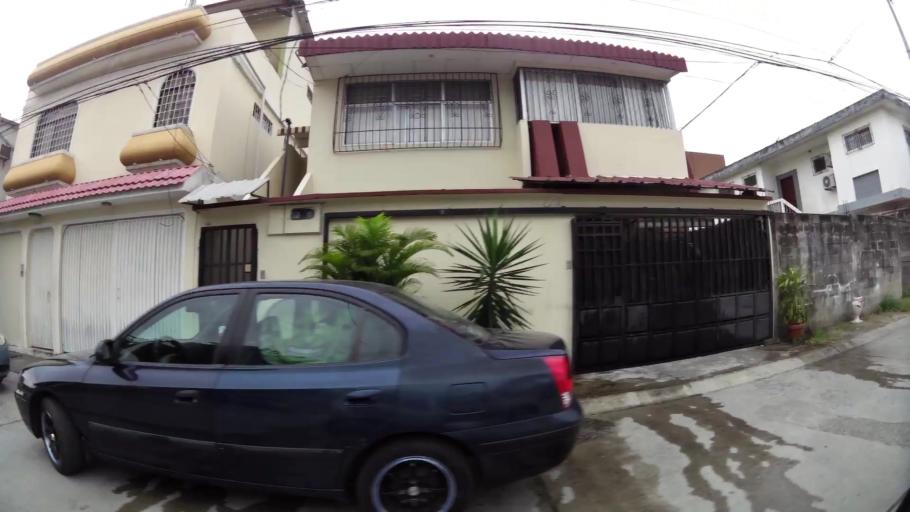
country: EC
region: Guayas
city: Eloy Alfaro
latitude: -2.1418
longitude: -79.9062
